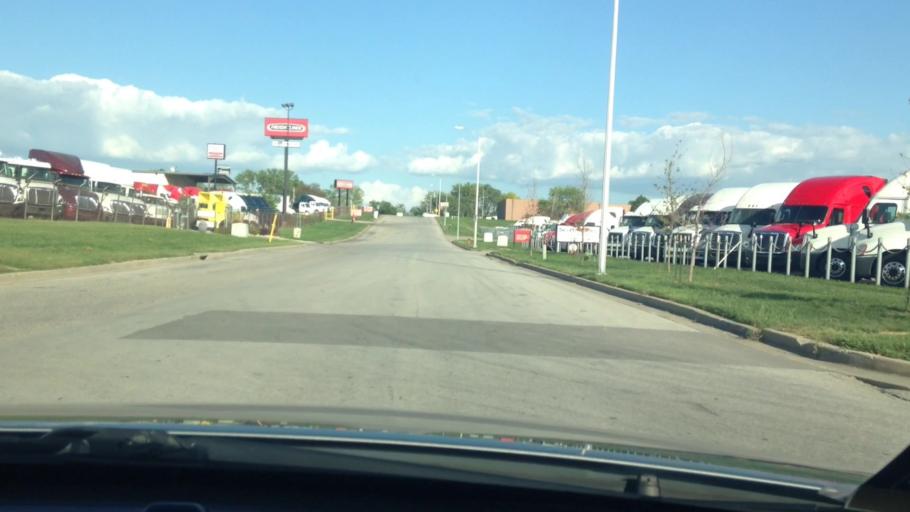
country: US
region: Missouri
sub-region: Clay County
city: Claycomo
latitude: 39.1636
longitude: -94.4917
